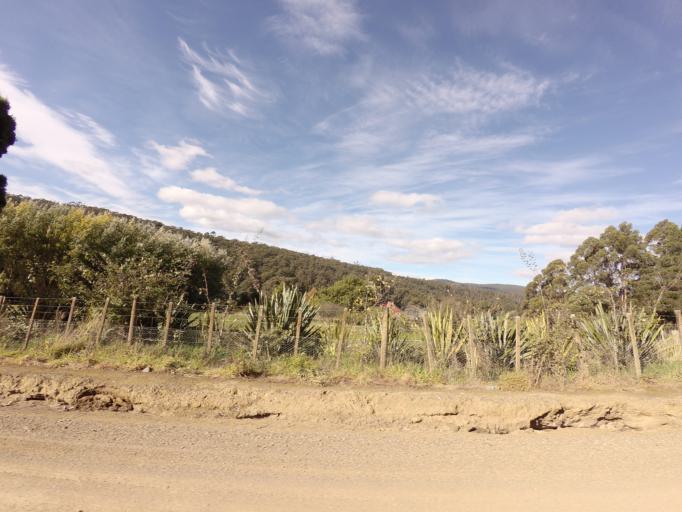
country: AU
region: Tasmania
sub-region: Clarence
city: Sandford
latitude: -43.1345
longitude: 147.7663
